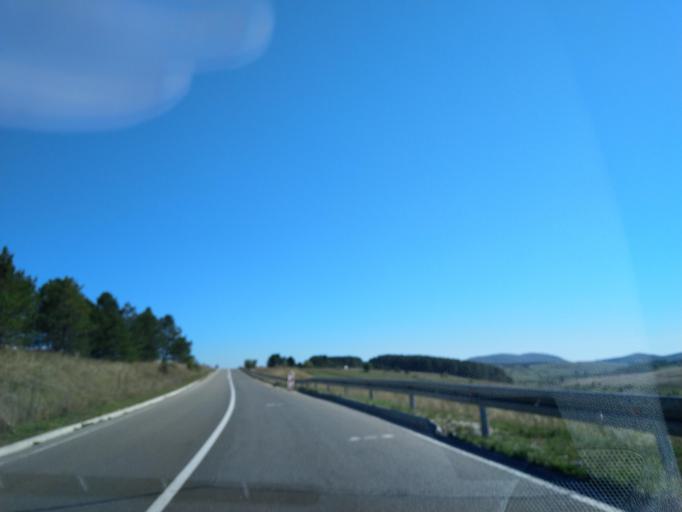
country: RS
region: Central Serbia
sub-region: Zlatiborski Okrug
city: Sjenica
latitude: 43.2666
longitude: 20.0368
